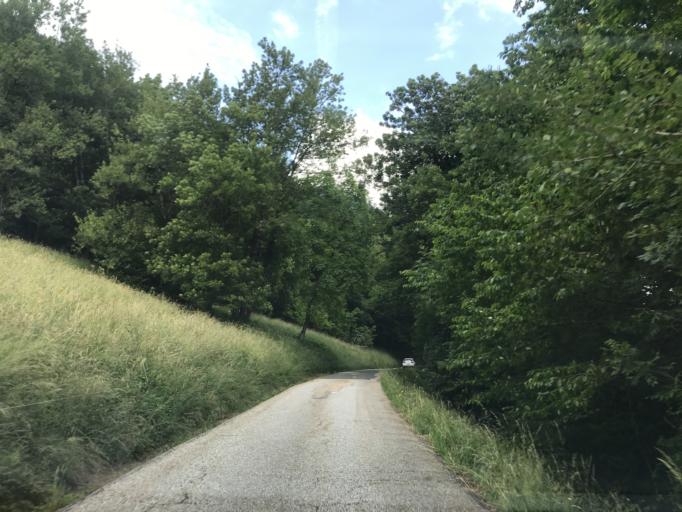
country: FR
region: Rhone-Alpes
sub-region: Departement de la Savoie
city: Mercury
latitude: 45.6746
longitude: 6.3187
